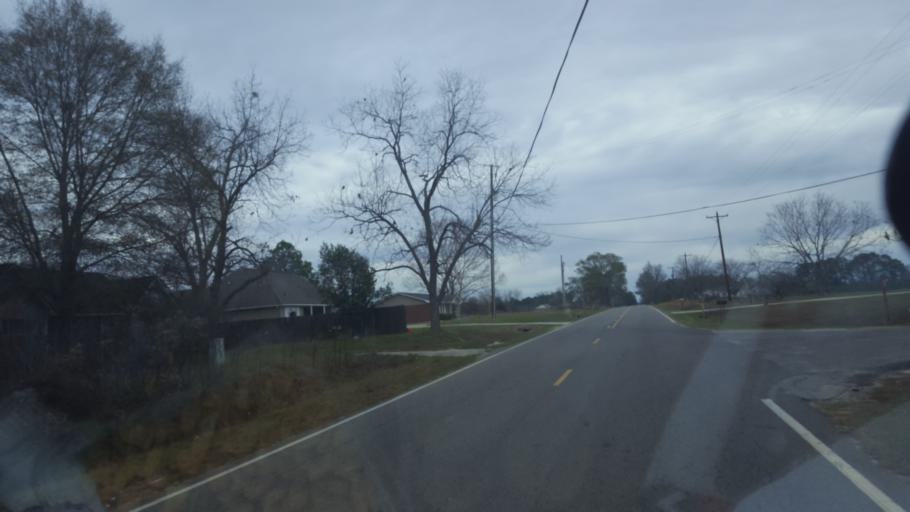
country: US
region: Georgia
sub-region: Ben Hill County
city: Fitzgerald
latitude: 31.7435
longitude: -83.2805
